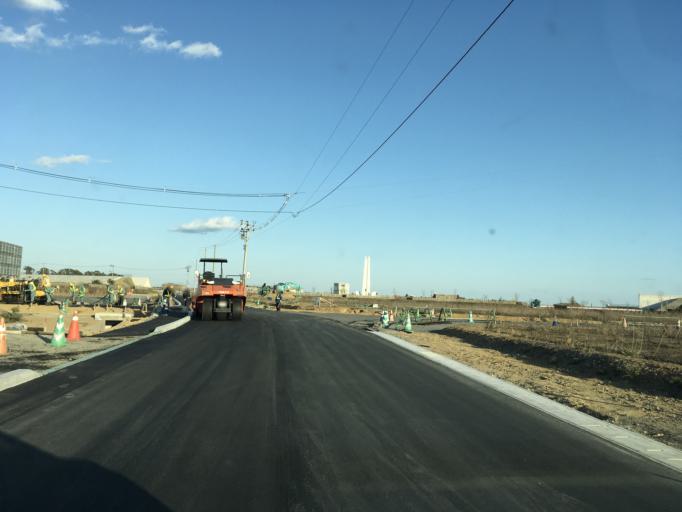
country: JP
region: Iwate
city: Ofunato
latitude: 38.8291
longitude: 141.5921
